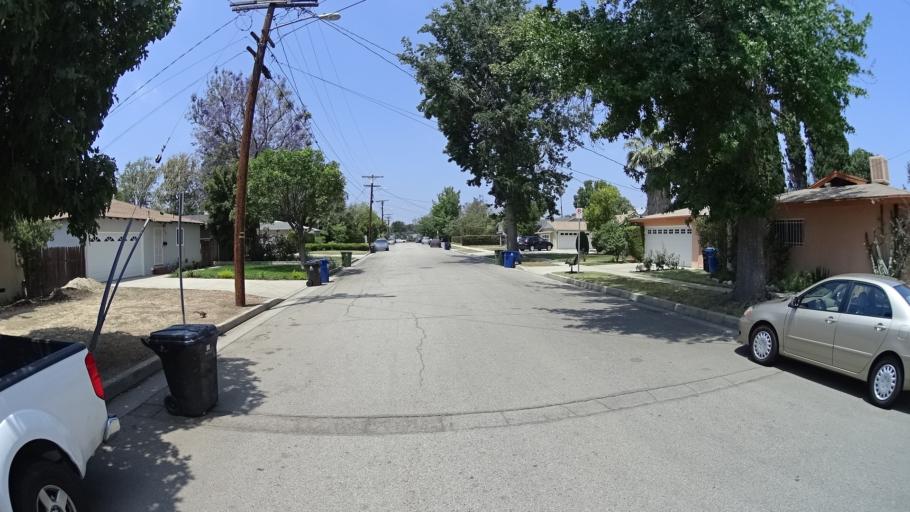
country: US
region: California
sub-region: Los Angeles County
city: Van Nuys
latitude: 34.1894
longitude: -118.4622
